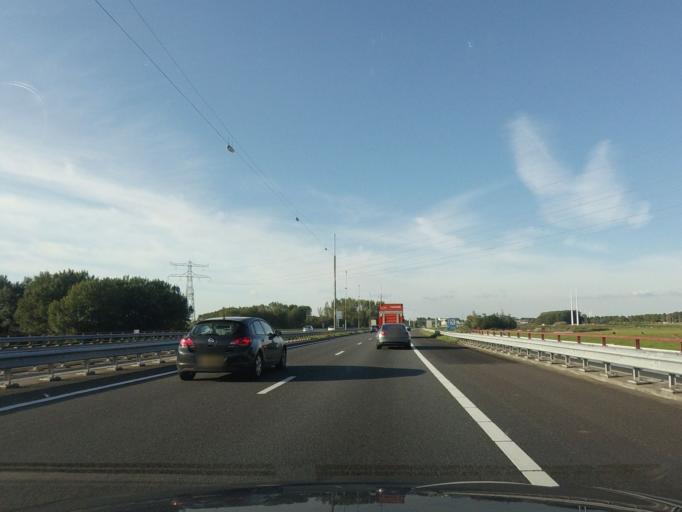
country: NL
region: North Holland
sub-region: Gemeente Velsen
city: Velsen-Zuid
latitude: 52.4457
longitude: 4.6671
